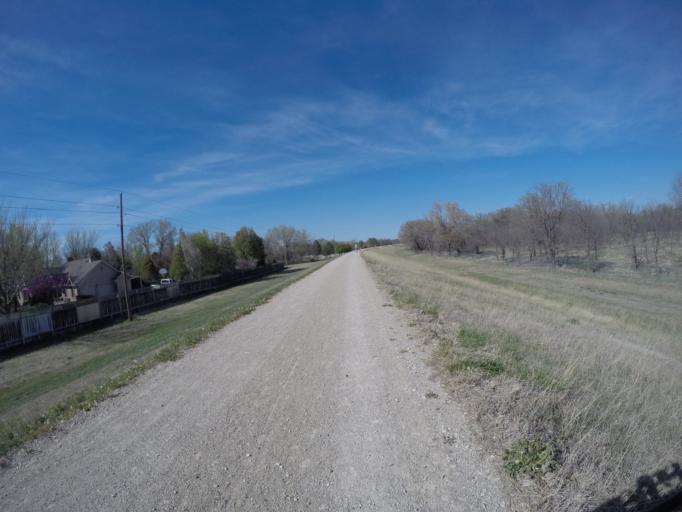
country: US
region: Kansas
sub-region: Saline County
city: Salina
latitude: 38.8099
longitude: -97.5846
